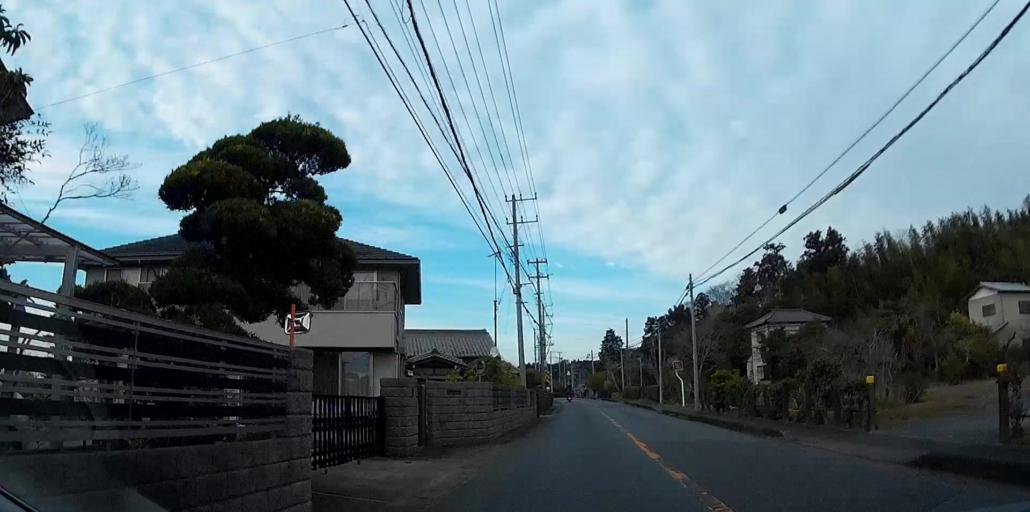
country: JP
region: Chiba
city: Kisarazu
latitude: 35.3719
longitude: 140.0602
